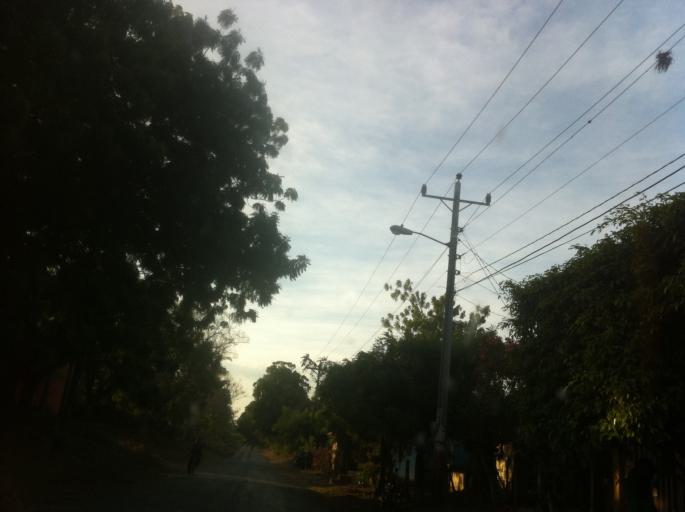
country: NI
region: Rivas
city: Potosi
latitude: 11.4938
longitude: -85.8598
